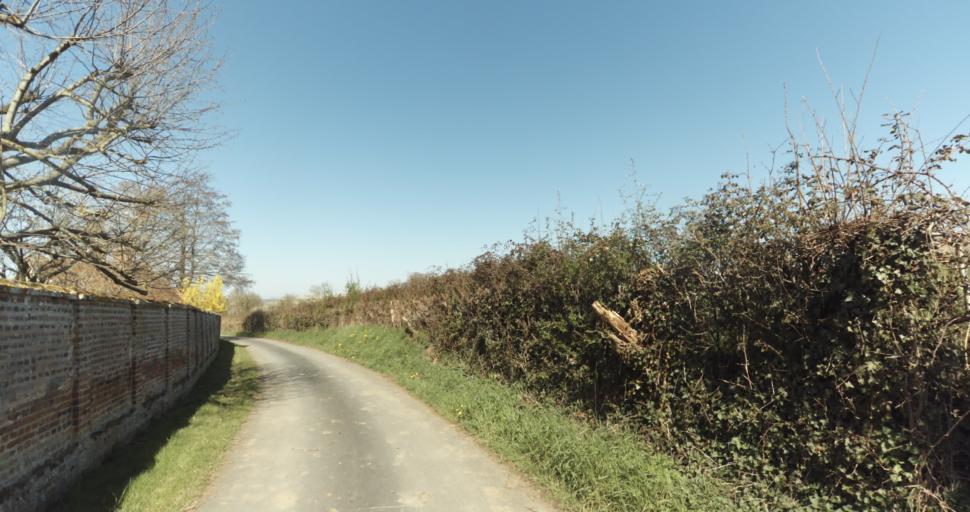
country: FR
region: Lower Normandy
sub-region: Departement du Calvados
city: Saint-Pierre-sur-Dives
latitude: 49.0185
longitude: 0.0437
